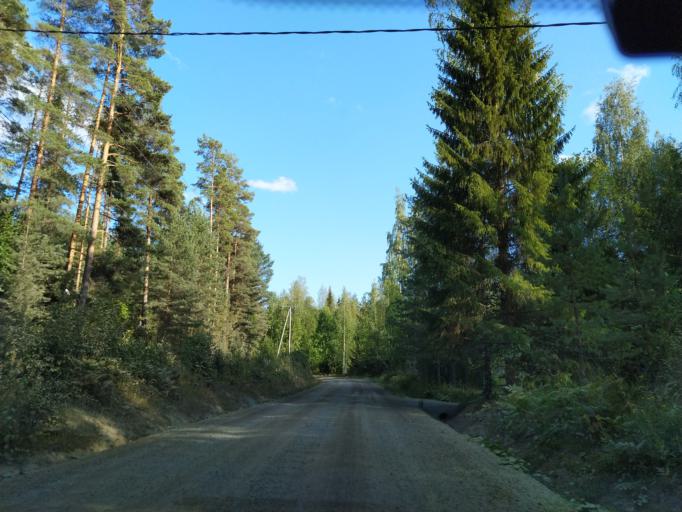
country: FI
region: Central Finland
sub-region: Jaemsae
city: Kuhmoinen
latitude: 61.7089
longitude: 24.9122
